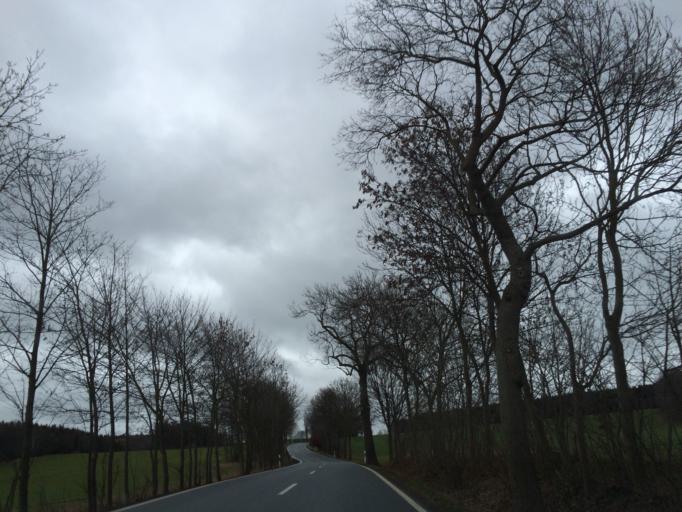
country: DE
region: Thuringia
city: Bodelwitz
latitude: 50.6670
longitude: 11.6204
